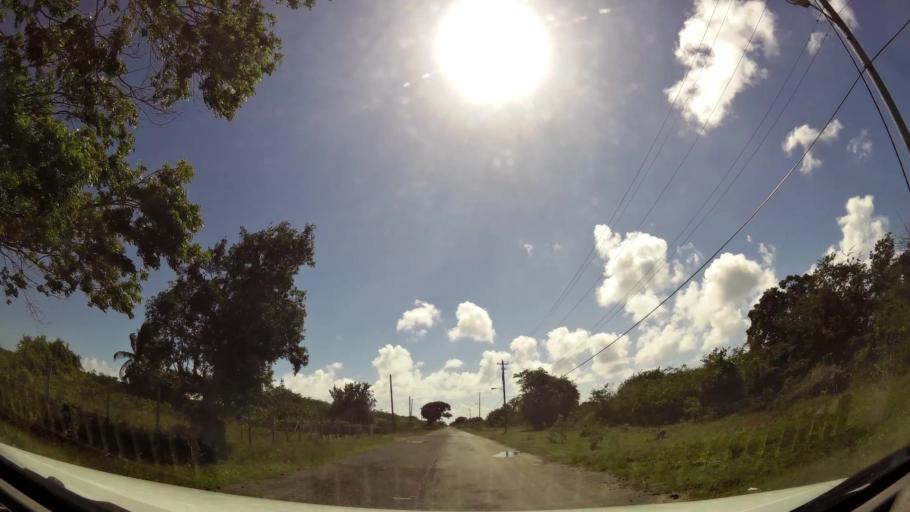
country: AG
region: Barbuda
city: Codrington
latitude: 17.6201
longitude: -61.8281
